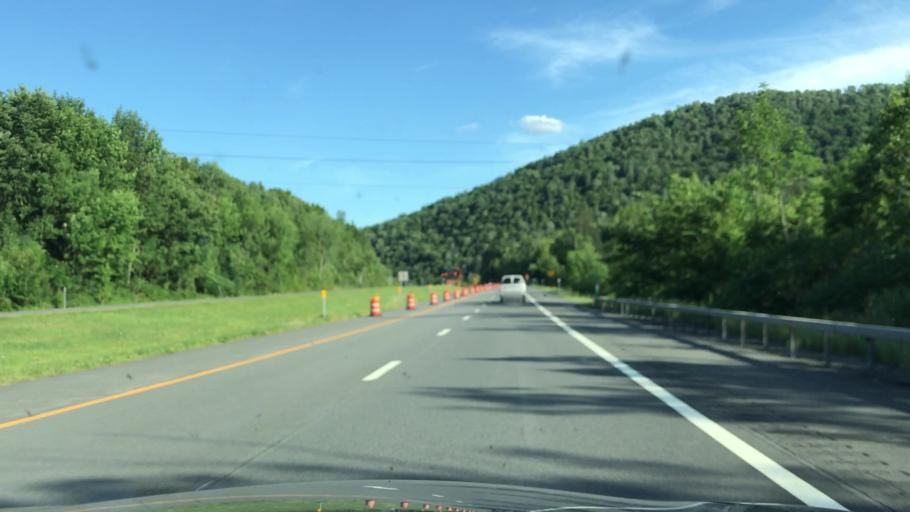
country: US
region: New York
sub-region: Delaware County
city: Walton
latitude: 41.9756
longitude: -75.0531
